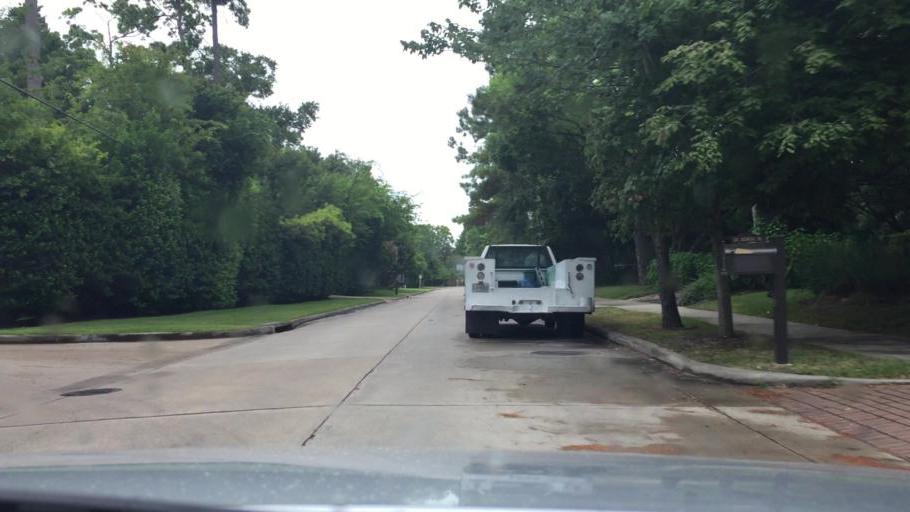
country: US
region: Texas
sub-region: Harris County
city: Piney Point Village
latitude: 29.7645
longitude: -95.5088
